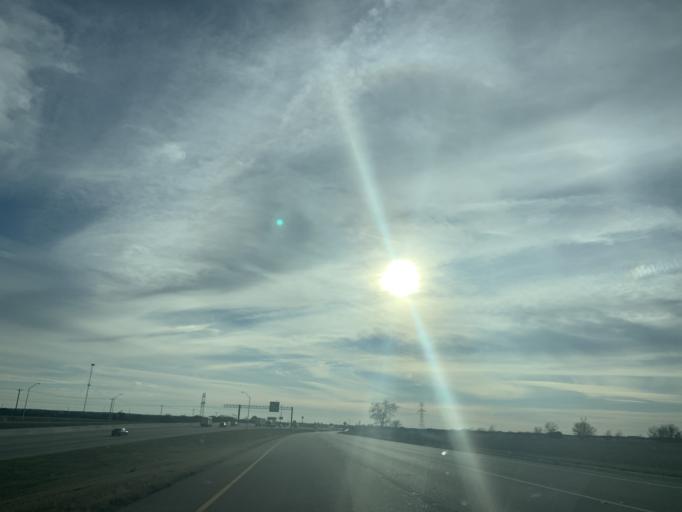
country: US
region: Texas
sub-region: Bell County
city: Salado
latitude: 30.9778
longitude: -97.5128
